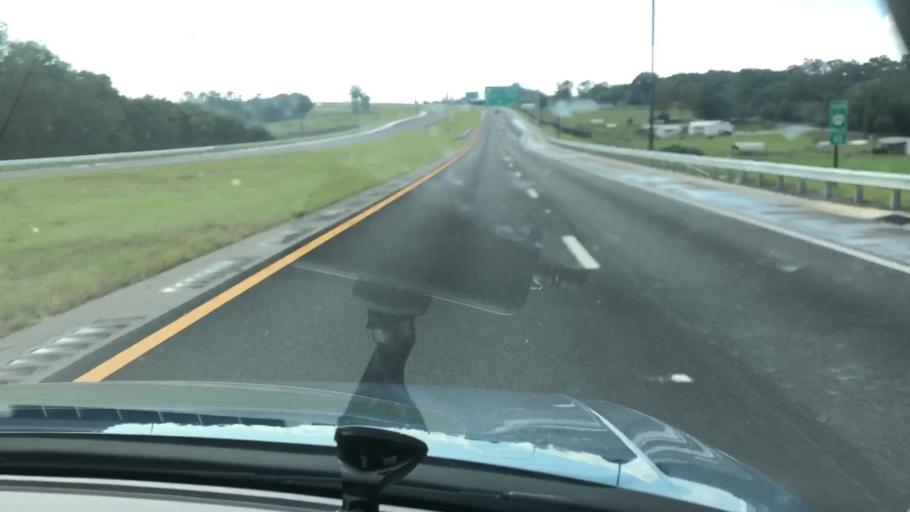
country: US
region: Florida
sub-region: Lake County
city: Mount Plymouth
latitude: 28.7758
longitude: -81.5489
